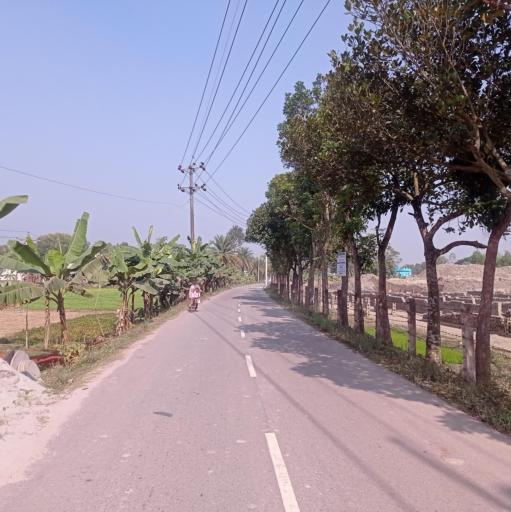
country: BD
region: Dhaka
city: Narsingdi
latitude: 24.0812
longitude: 90.6943
